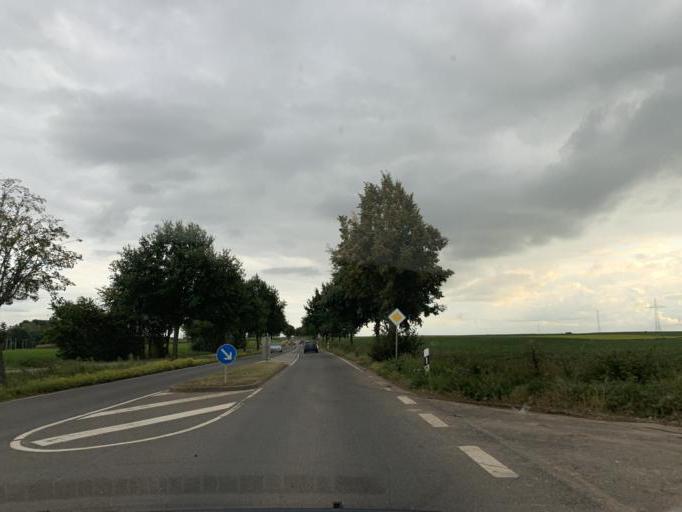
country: DE
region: North Rhine-Westphalia
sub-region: Regierungsbezirk Koln
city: Linnich
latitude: 50.9963
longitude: 6.2534
